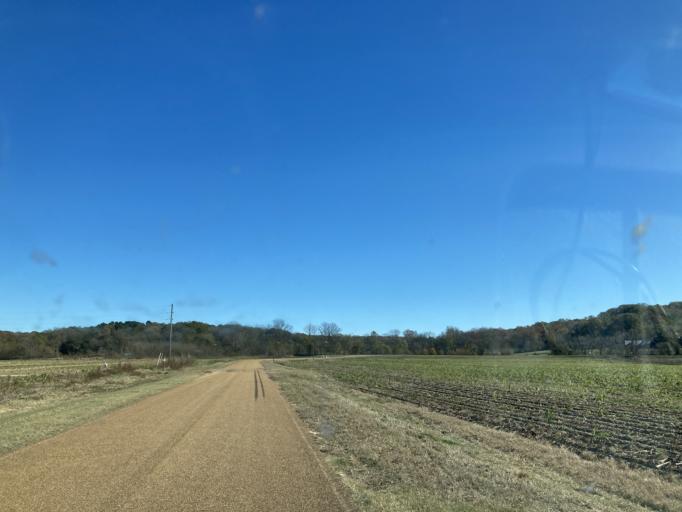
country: US
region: Mississippi
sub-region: Hinds County
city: Lynchburg
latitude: 32.6257
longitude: -90.5763
